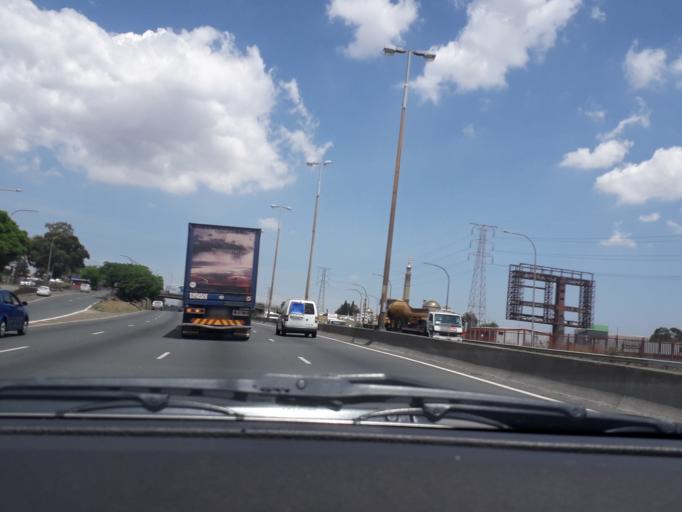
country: ZA
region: Gauteng
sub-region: City of Johannesburg Metropolitan Municipality
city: Johannesburg
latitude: -26.2427
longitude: 28.0088
